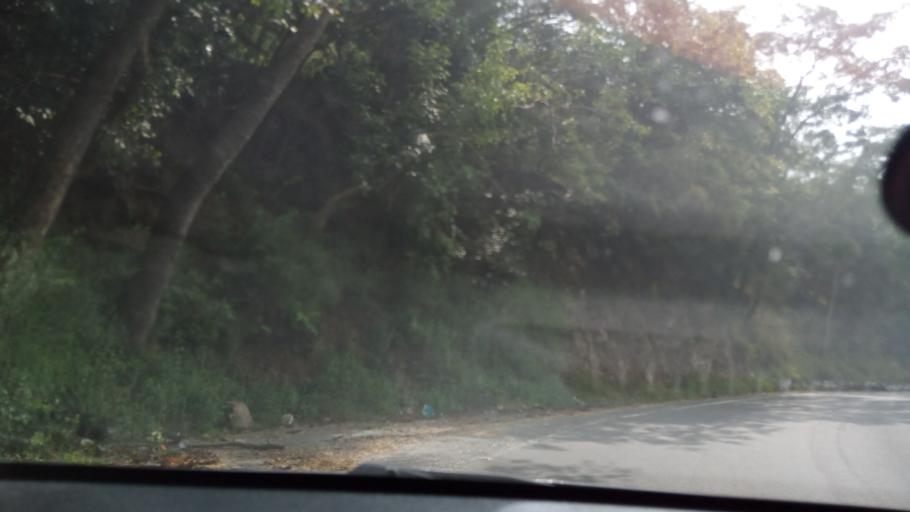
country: IN
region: Tamil Nadu
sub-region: Erode
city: Sathyamangalam
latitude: 11.6023
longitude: 77.1277
